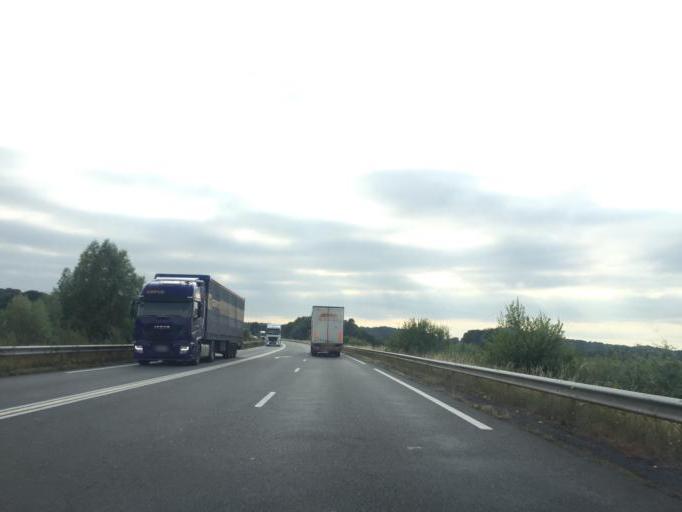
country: FR
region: Auvergne
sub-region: Departement de l'Allier
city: Dompierre-sur-Besbre
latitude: 46.5409
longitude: 3.6778
